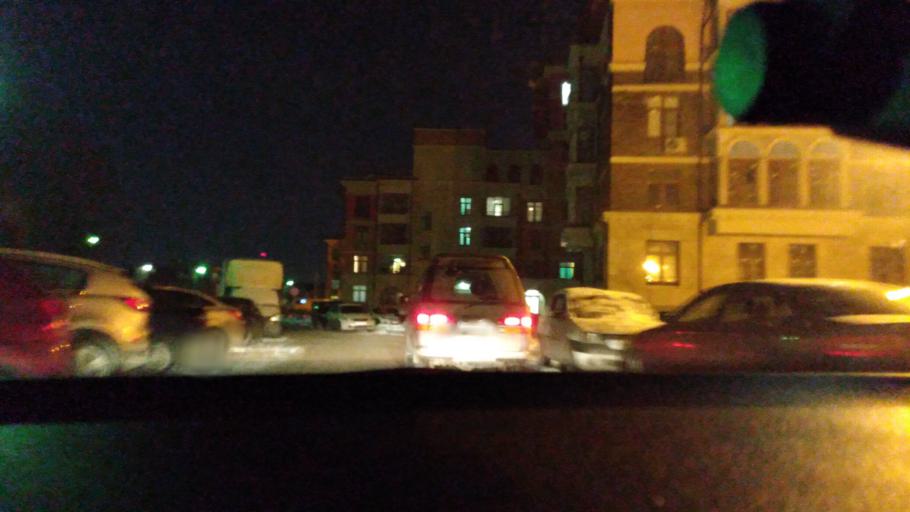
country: RU
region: Moskovskaya
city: Opalikha
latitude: 55.8190
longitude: 37.2489
